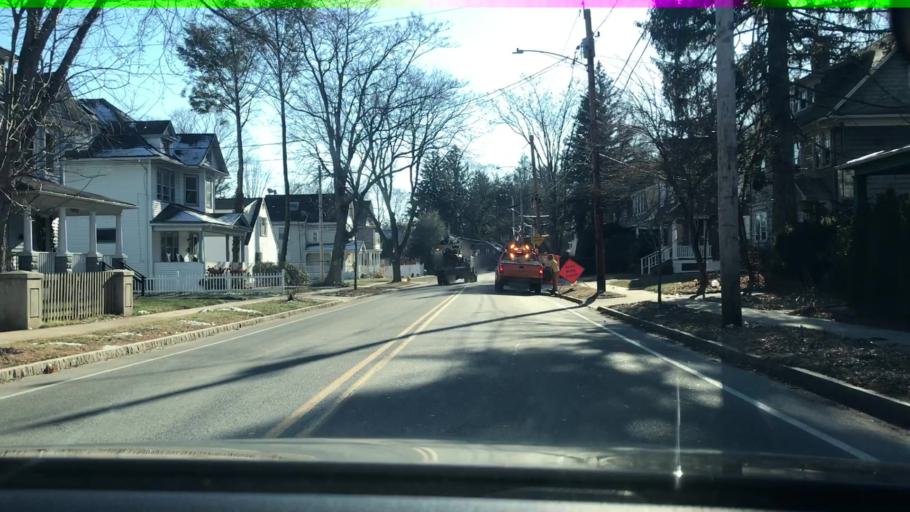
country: US
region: Connecticut
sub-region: New Haven County
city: New Haven
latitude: 41.3258
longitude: -72.9685
